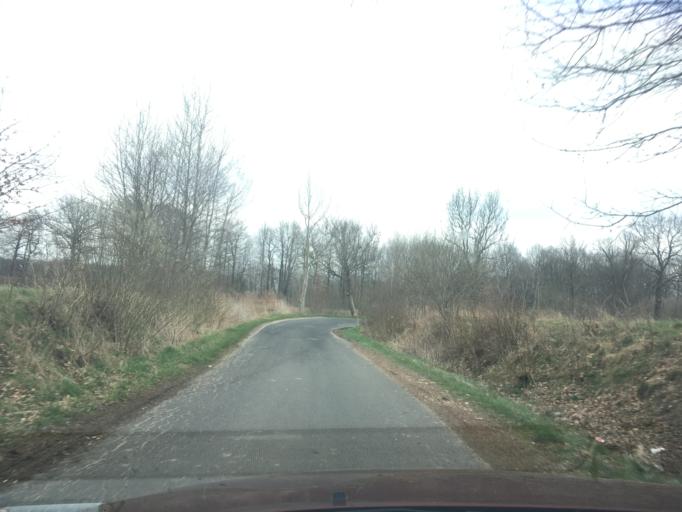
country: PL
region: Lower Silesian Voivodeship
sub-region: Powiat zgorzelecki
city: Lagow
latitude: 51.1749
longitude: 15.0431
